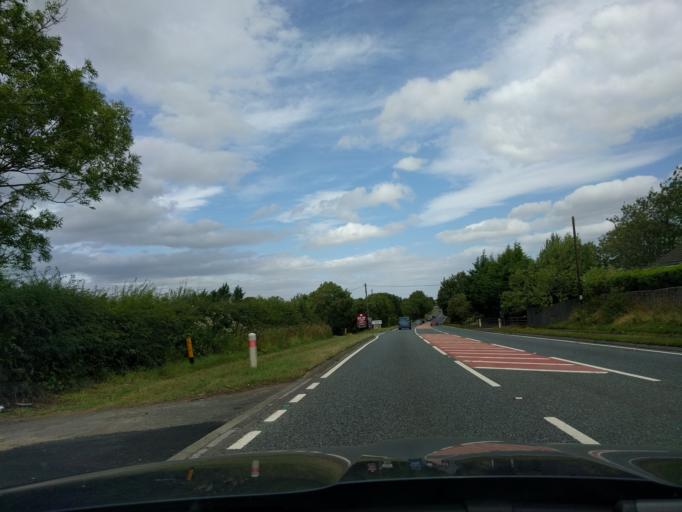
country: GB
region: England
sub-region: Northumberland
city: Felton
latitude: 55.2430
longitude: -1.7037
